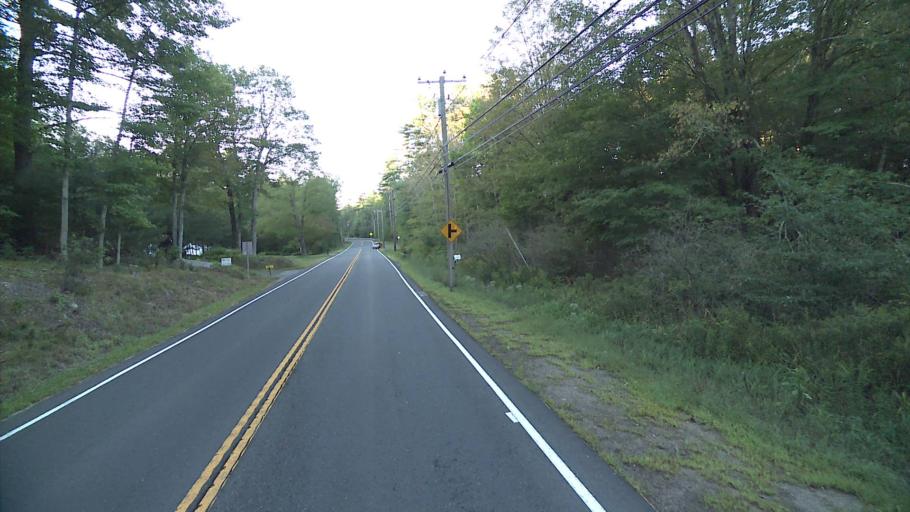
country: US
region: Connecticut
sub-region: Tolland County
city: Stafford
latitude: 41.9832
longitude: -72.3163
